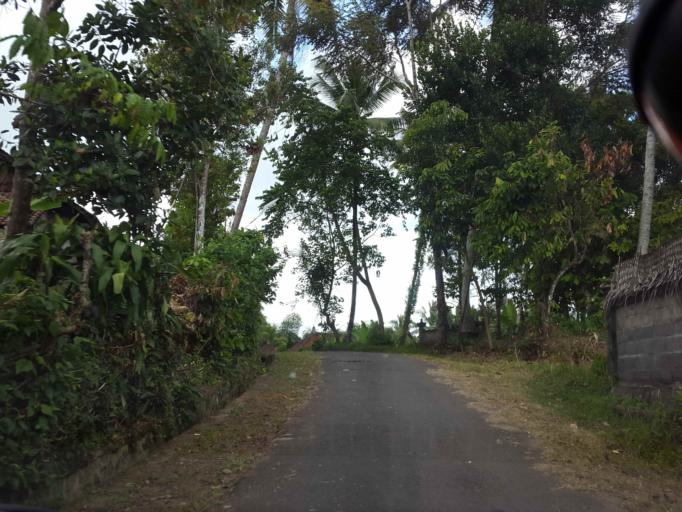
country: ID
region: Bali
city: Banjar Kelodan
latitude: -8.4946
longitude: 115.3688
